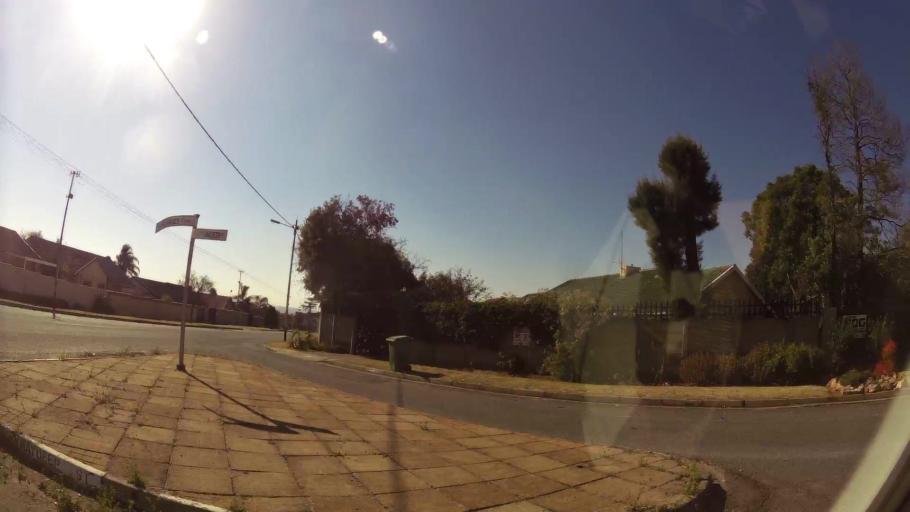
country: ZA
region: Gauteng
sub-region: Ekurhuleni Metropolitan Municipality
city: Germiston
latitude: -26.2540
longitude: 28.1017
